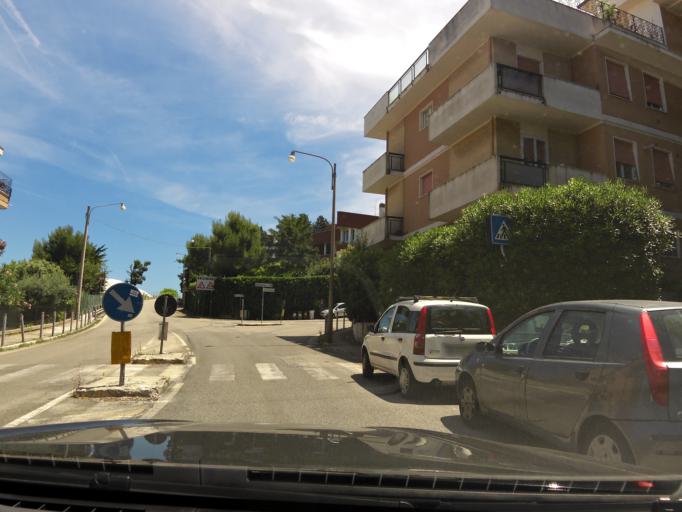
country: IT
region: The Marches
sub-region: Provincia di Ancona
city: Pietra la Croce
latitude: 43.6118
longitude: 13.5305
